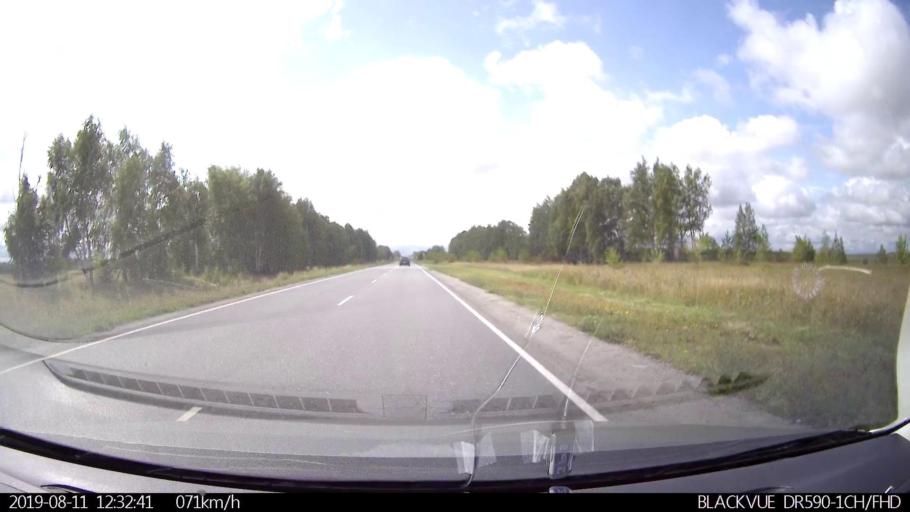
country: RU
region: Ulyanovsk
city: Ignatovka
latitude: 53.8120
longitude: 47.8632
